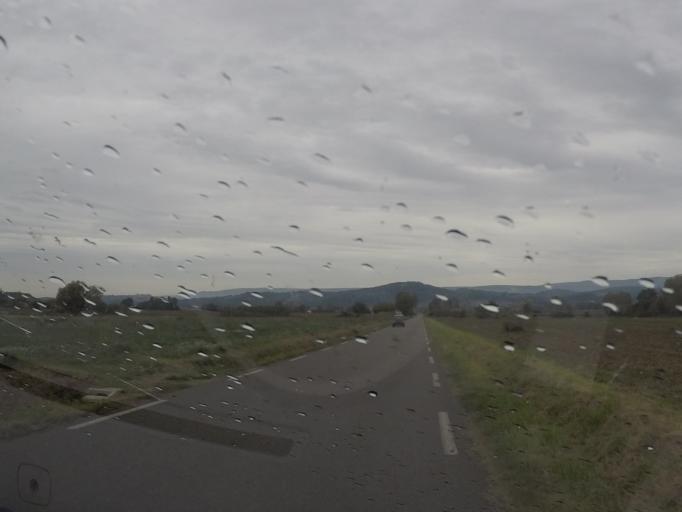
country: FR
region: Provence-Alpes-Cote d'Azur
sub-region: Departement du Vaucluse
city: Bonnieux
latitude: 43.8402
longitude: 5.2901
